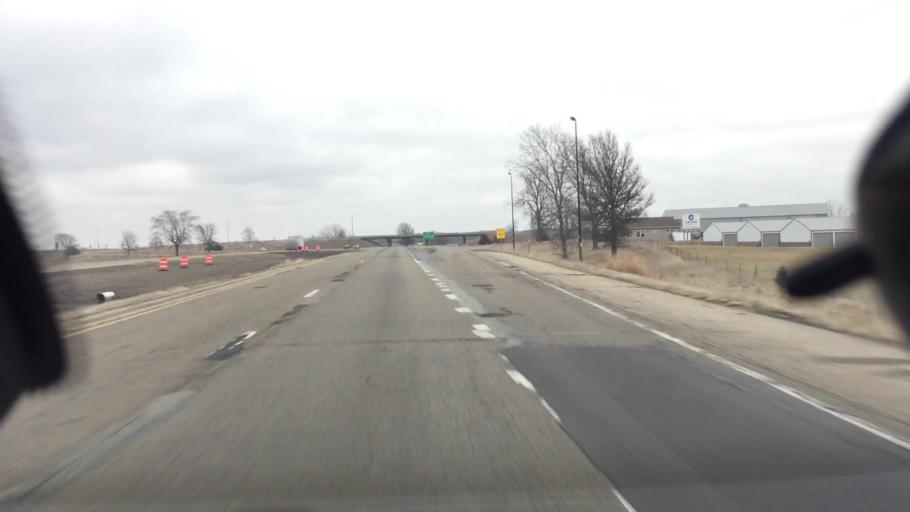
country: US
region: Illinois
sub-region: Woodford County
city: Eureka
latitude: 40.6224
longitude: -89.2808
